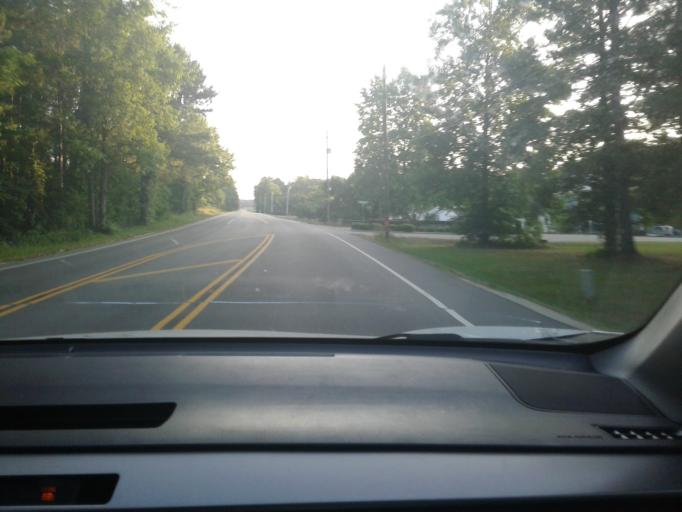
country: US
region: North Carolina
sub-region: Harnett County
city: Lillington
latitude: 35.4656
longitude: -78.8286
